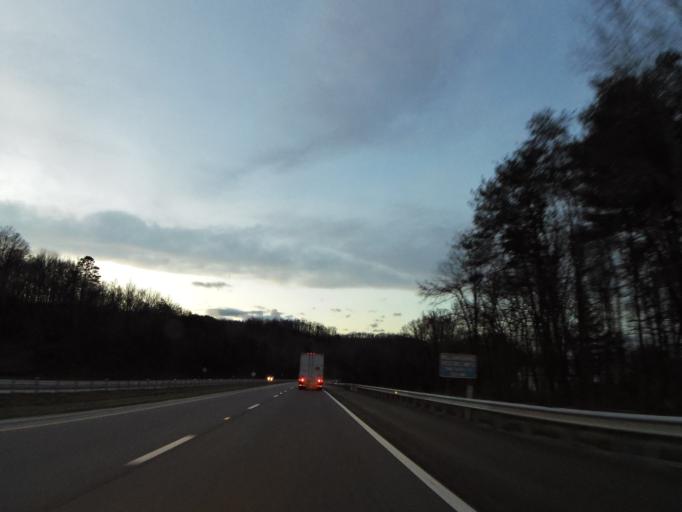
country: US
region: Kentucky
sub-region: Whitley County
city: Williamsburg
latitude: 36.7008
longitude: -84.1460
